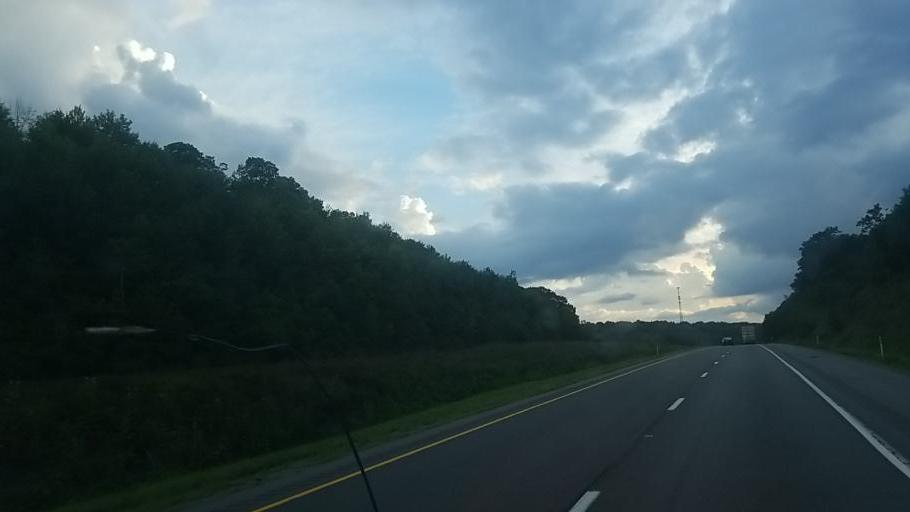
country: US
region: Pennsylvania
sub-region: Clearfield County
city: Treasure Lake
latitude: 41.1212
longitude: -78.6230
